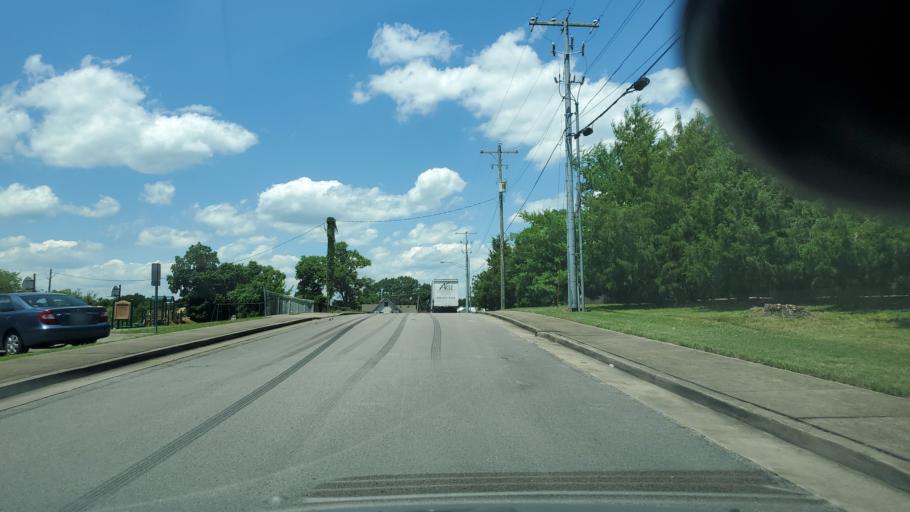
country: US
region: Tennessee
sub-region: Davidson County
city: Nashville
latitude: 36.1914
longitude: -86.7469
